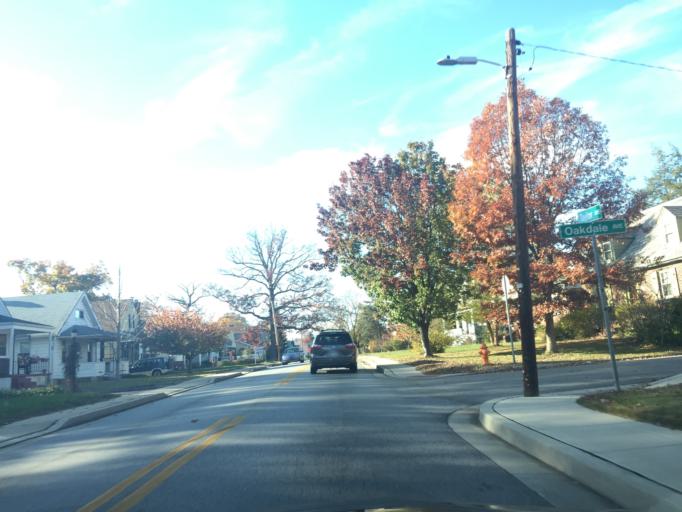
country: US
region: Maryland
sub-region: Baltimore County
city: Parkville
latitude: 39.3773
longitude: -76.5500
